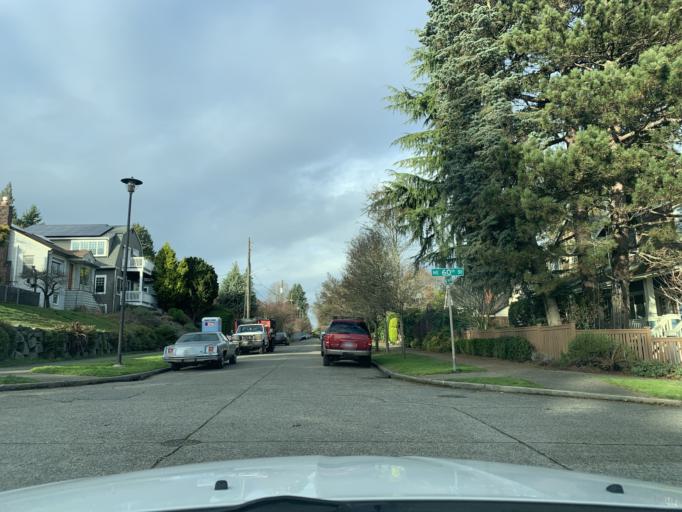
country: US
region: Washington
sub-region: King County
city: Inglewood-Finn Hill
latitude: 47.6721
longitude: -122.2890
